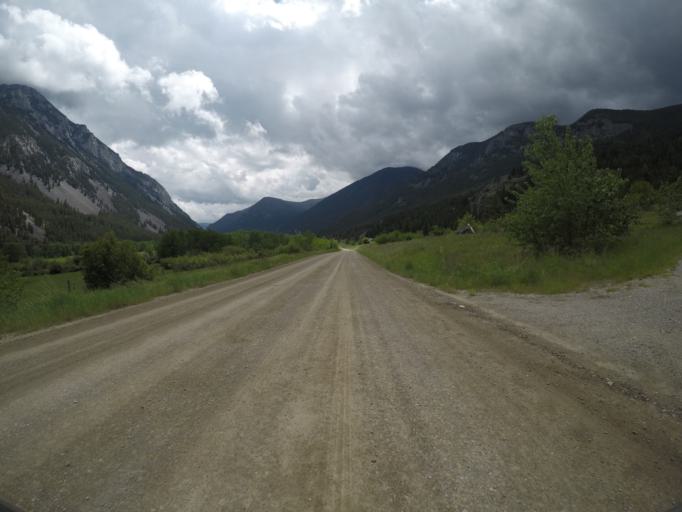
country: US
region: Montana
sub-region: Park County
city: Livingston
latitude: 45.5192
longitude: -110.2256
